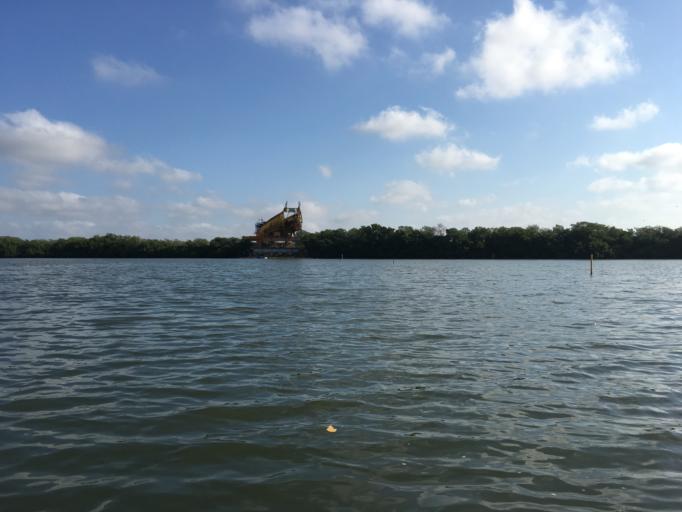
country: CO
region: Bolivar
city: Cartagena
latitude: 10.4880
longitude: -75.4817
